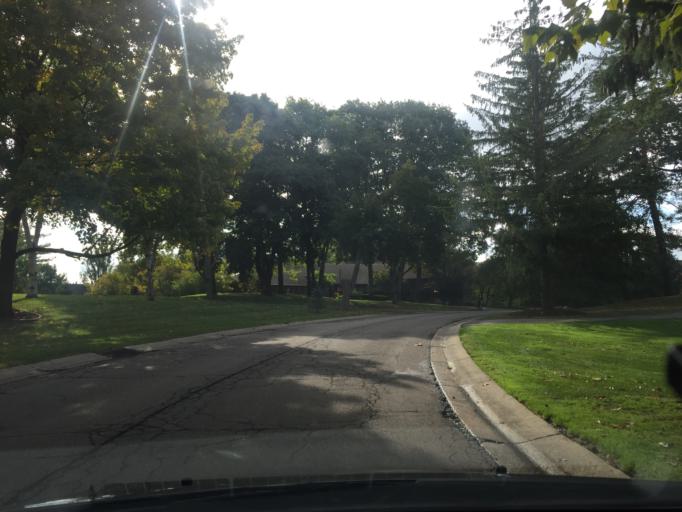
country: US
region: Michigan
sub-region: Oakland County
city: Sylvan Lake
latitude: 42.5868
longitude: -83.3104
